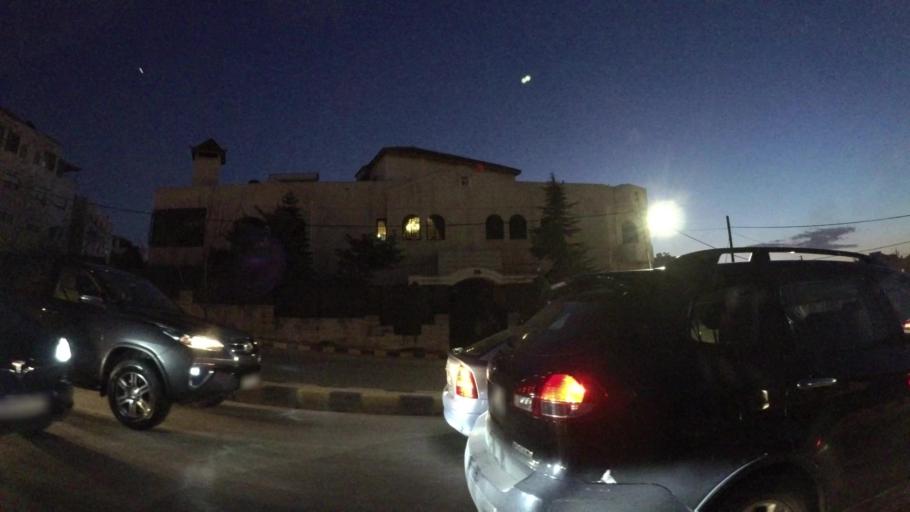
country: JO
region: Amman
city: Al Jubayhah
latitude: 31.9798
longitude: 35.8676
